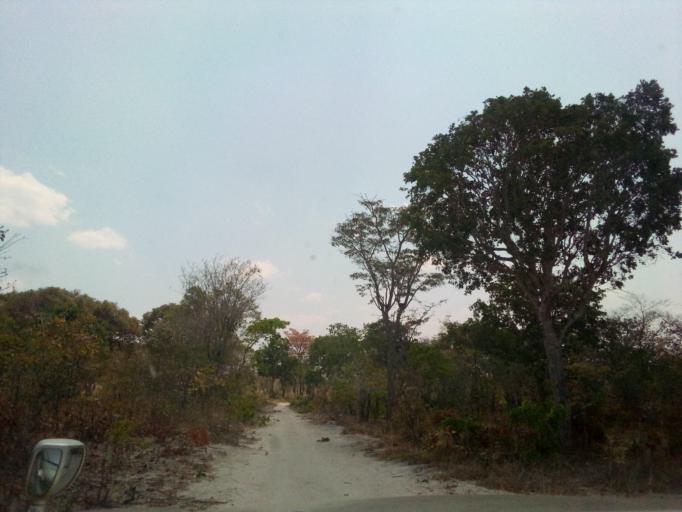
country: ZM
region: Northern
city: Chinsali
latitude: -10.8032
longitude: 31.7886
